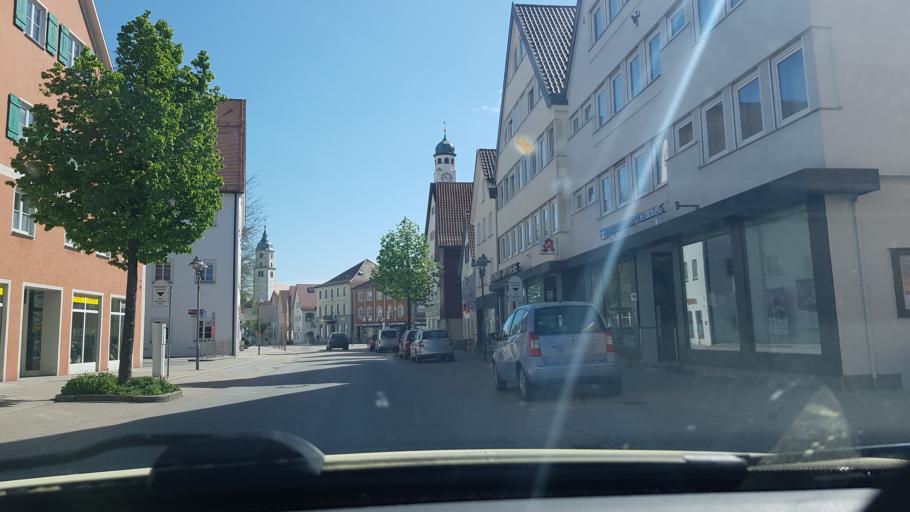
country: DE
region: Baden-Wuerttemberg
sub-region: Tuebingen Region
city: Bad Wurzach
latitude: 47.9083
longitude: 9.8953
